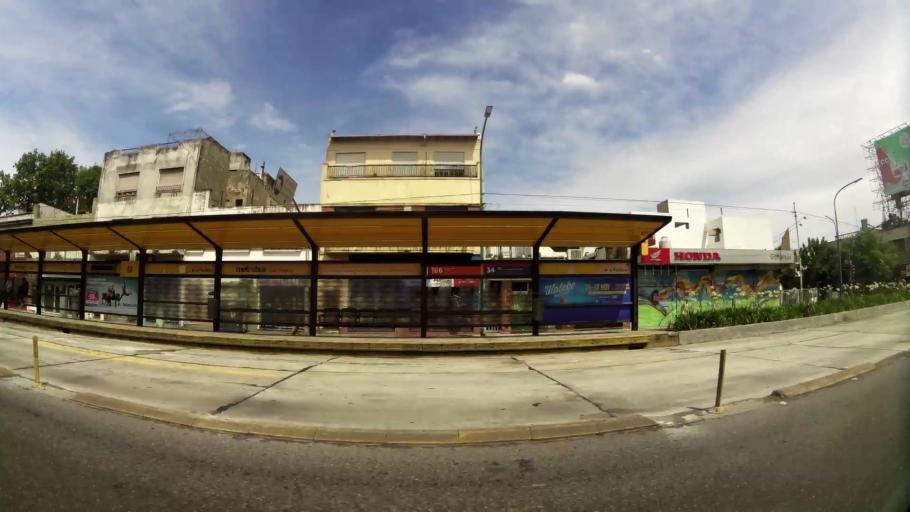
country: AR
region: Buenos Aires F.D.
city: Villa Santa Rita
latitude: -34.6298
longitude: -58.4953
